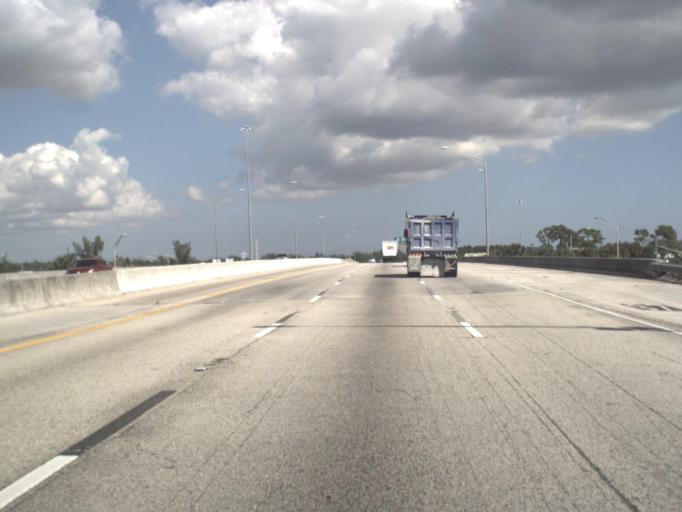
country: US
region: Florida
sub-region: Palm Beach County
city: Lake Belvedere Estates
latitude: 26.6782
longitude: -80.1671
